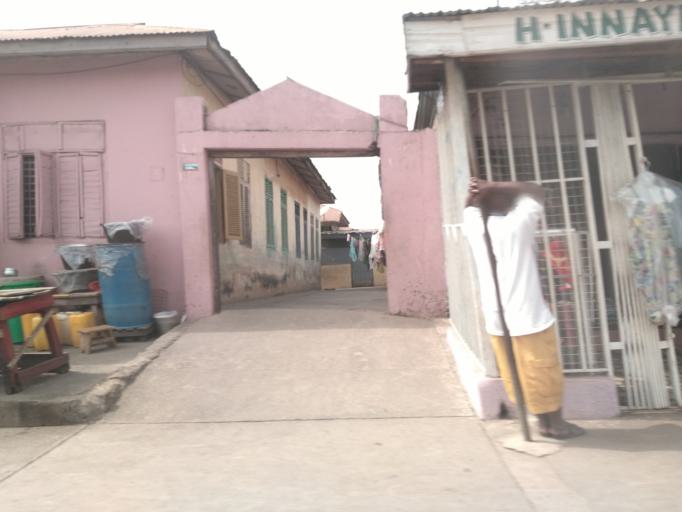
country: GH
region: Ashanti
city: Kumasi
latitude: 6.6949
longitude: -1.5942
